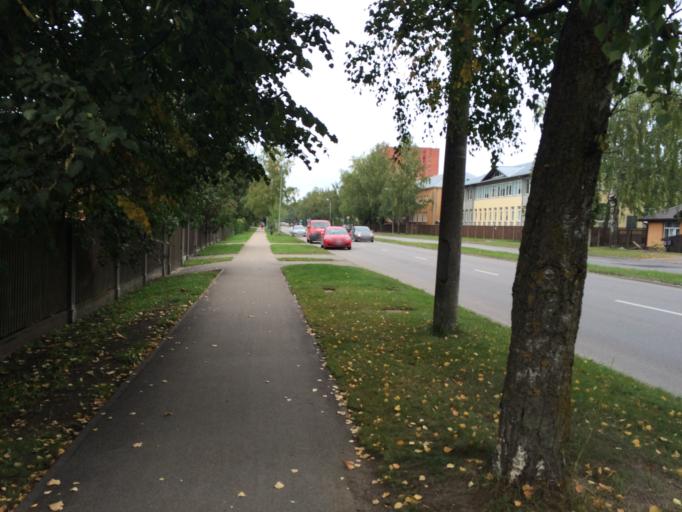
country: LV
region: Riga
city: Jaunciems
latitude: 56.9725
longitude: 24.1915
